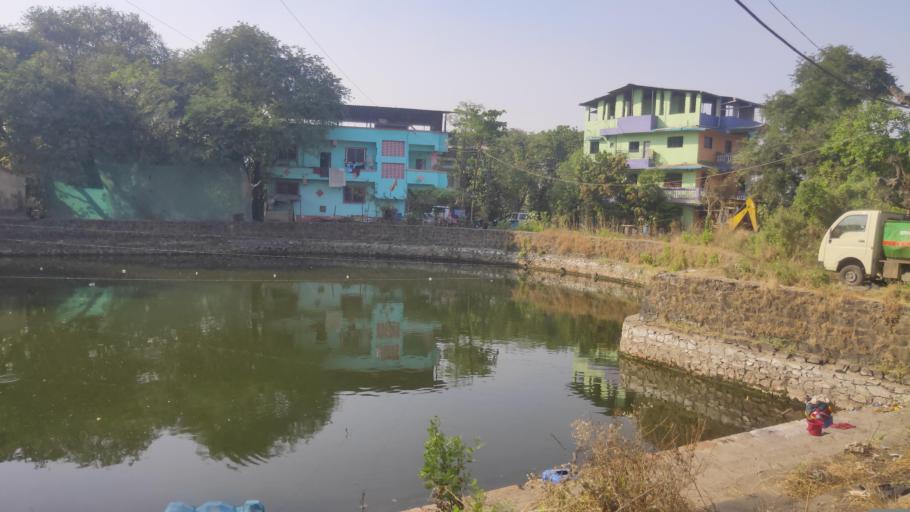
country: IN
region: Maharashtra
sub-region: Thane
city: Dombivli
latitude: 19.2159
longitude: 73.0387
